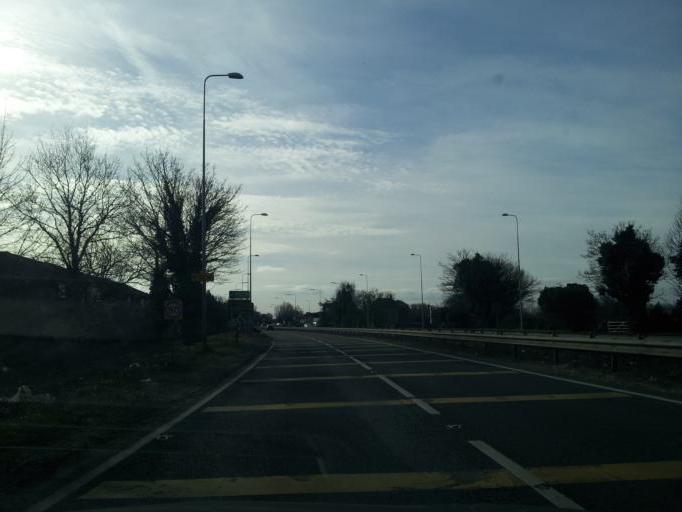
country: GB
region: England
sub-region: Central Bedfordshire
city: Sandy
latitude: 52.1303
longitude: -0.3005
